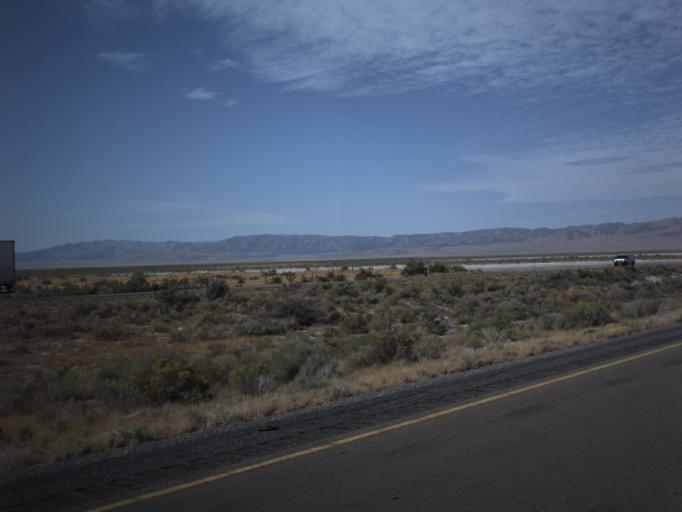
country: US
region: Utah
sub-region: Tooele County
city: Grantsville
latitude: 40.7497
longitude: -112.6888
